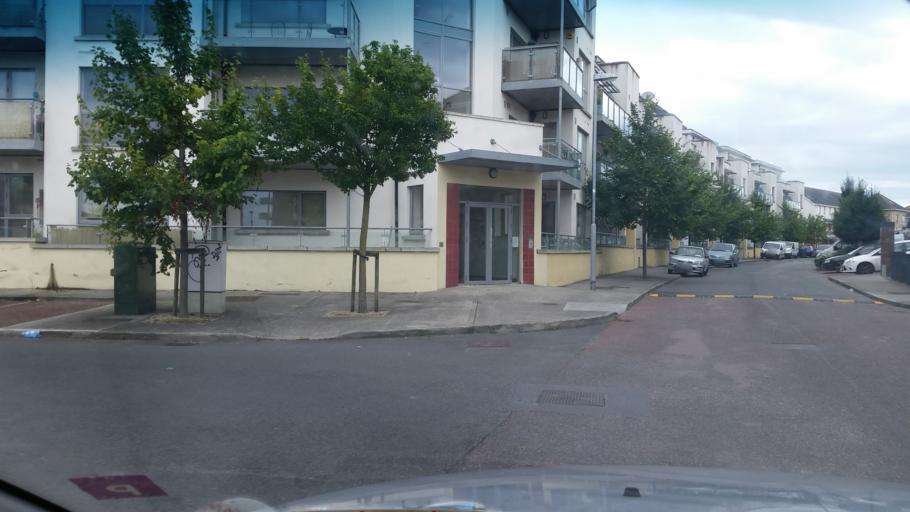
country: IE
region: Leinster
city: Donaghmede
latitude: 53.4015
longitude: -6.1509
